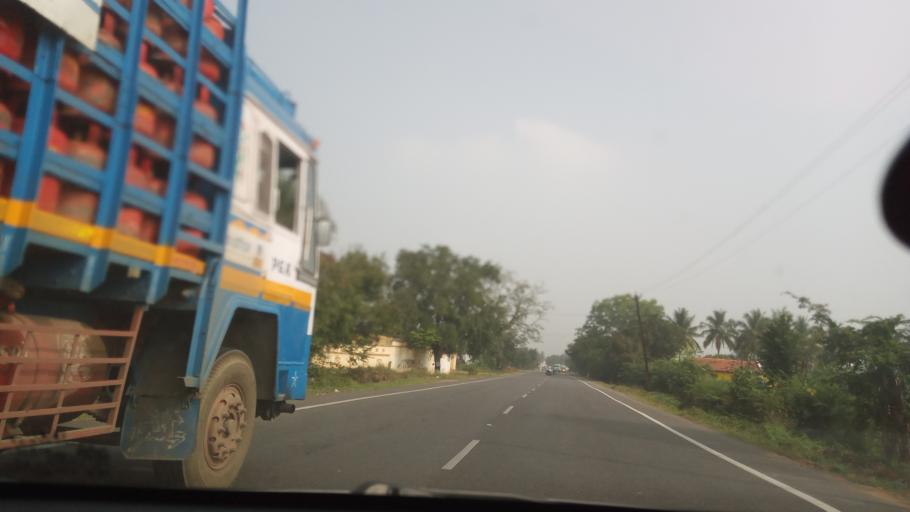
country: IN
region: Tamil Nadu
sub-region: Erode
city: Punjai Puliyampatti
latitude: 11.3736
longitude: 77.1714
